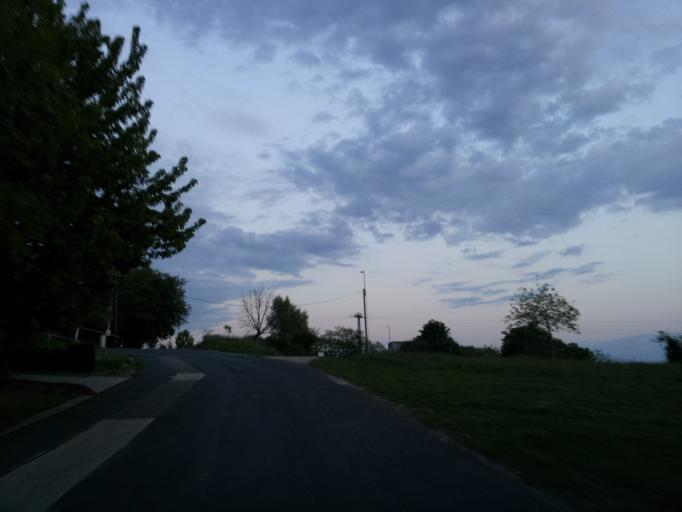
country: HU
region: Komarom-Esztergom
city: Csolnok
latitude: 47.6858
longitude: 18.7210
